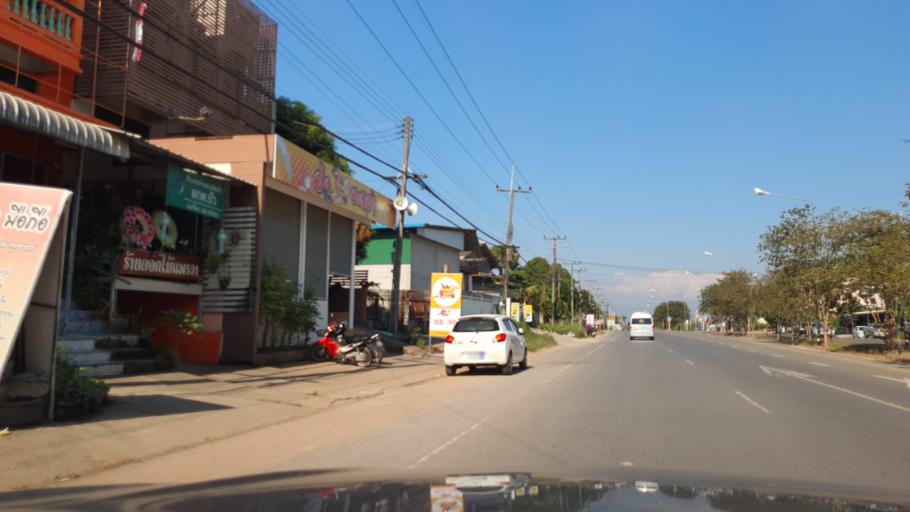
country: TH
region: Nan
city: Pua
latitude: 19.1710
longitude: 100.9204
